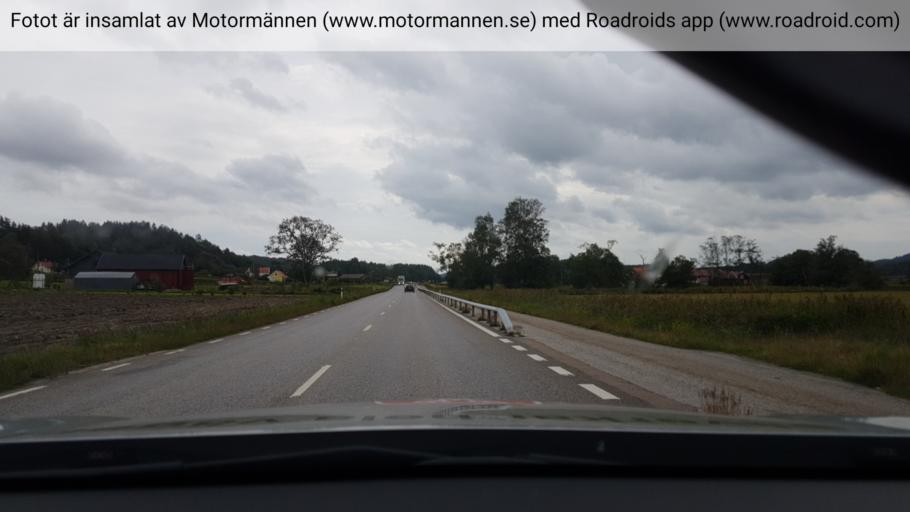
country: SE
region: Vaestra Goetaland
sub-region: Munkedals Kommun
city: Munkedal
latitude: 58.5119
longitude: 11.5756
